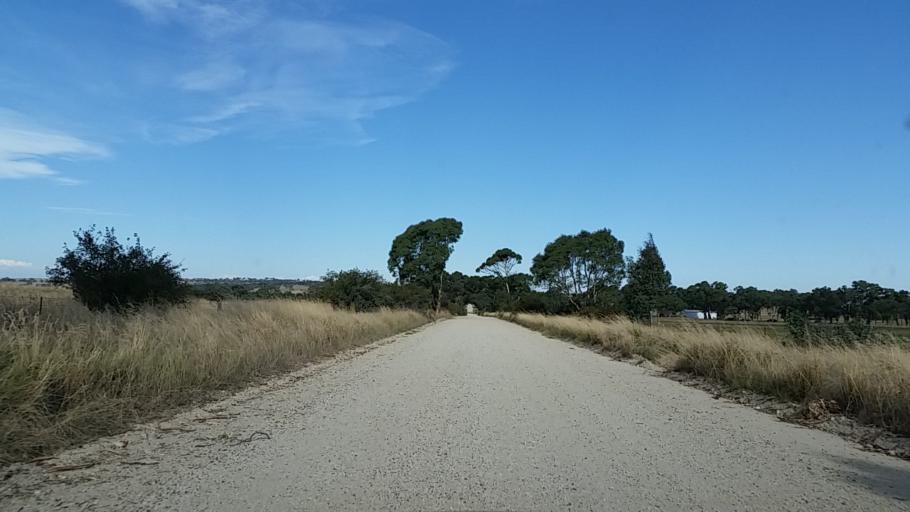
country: AU
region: South Australia
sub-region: Barossa
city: Angaston
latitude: -34.5799
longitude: 139.1437
